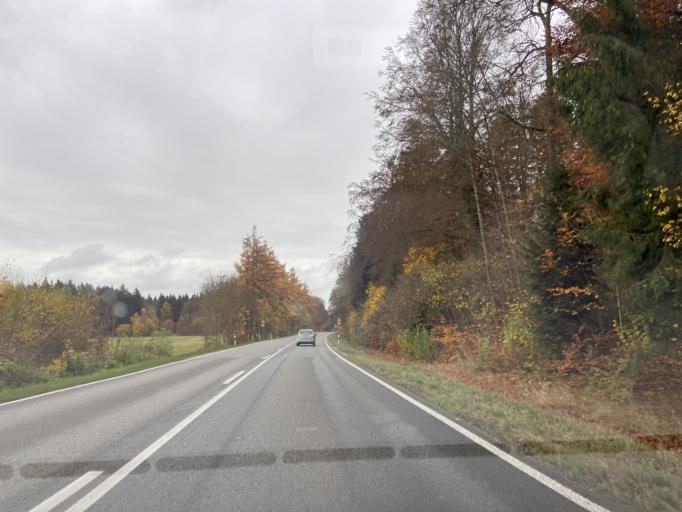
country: DE
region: Baden-Wuerttemberg
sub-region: Tuebingen Region
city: Sigmaringen
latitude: 48.0580
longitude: 9.2305
